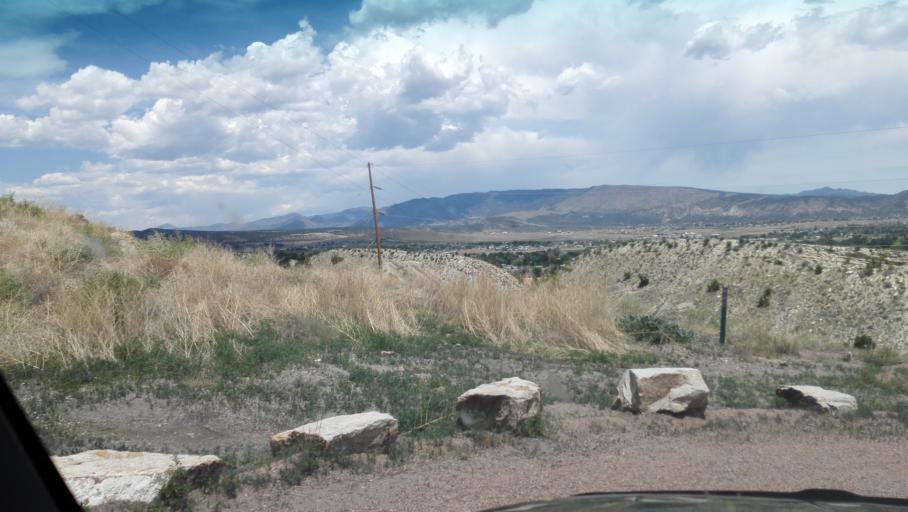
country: US
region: Colorado
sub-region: Fremont County
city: Canon City
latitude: 38.4499
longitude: -105.2479
